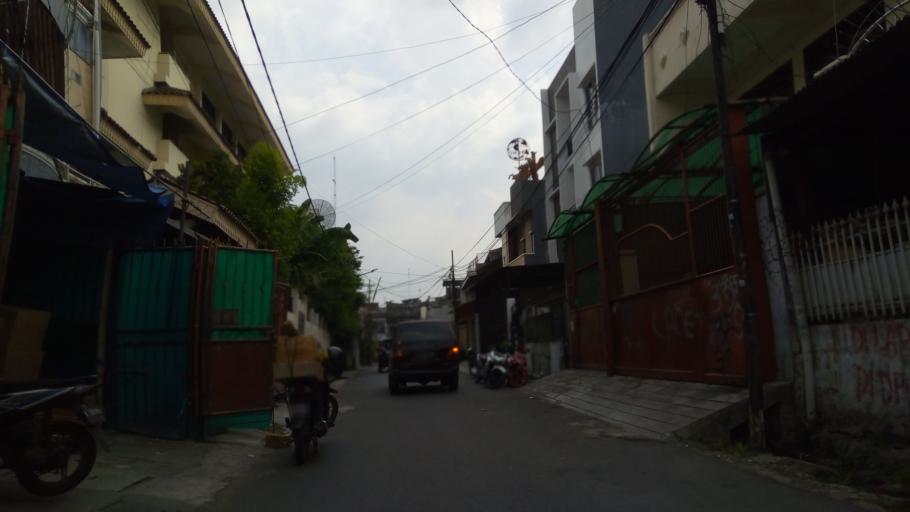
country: ID
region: Jakarta Raya
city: Jakarta
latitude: -6.1587
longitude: 106.8330
